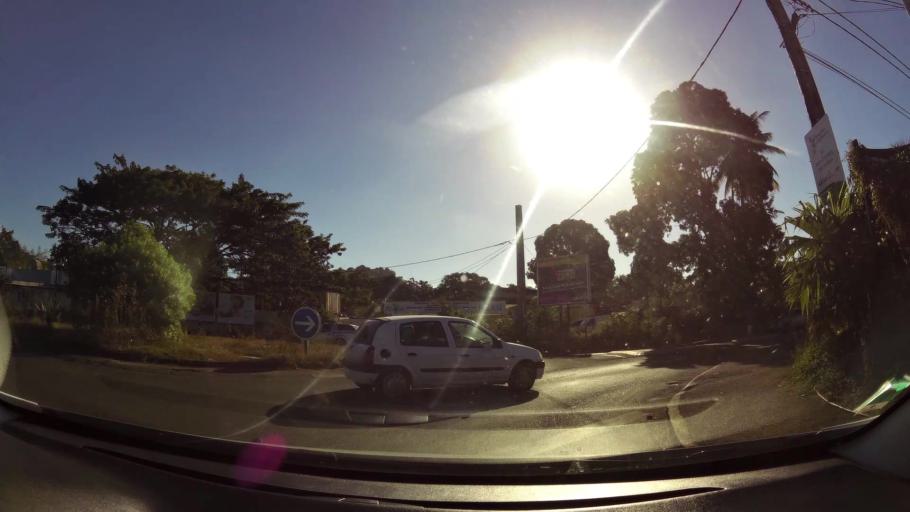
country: YT
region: Mamoudzou
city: Mamoudzou
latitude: -12.7636
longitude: 45.2258
